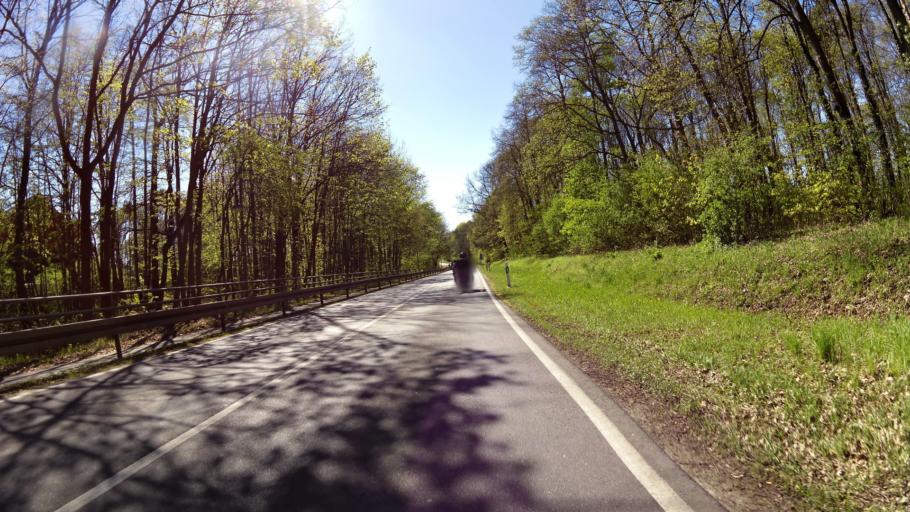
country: DE
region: Brandenburg
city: Bernau bei Berlin
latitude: 52.6949
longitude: 13.5547
